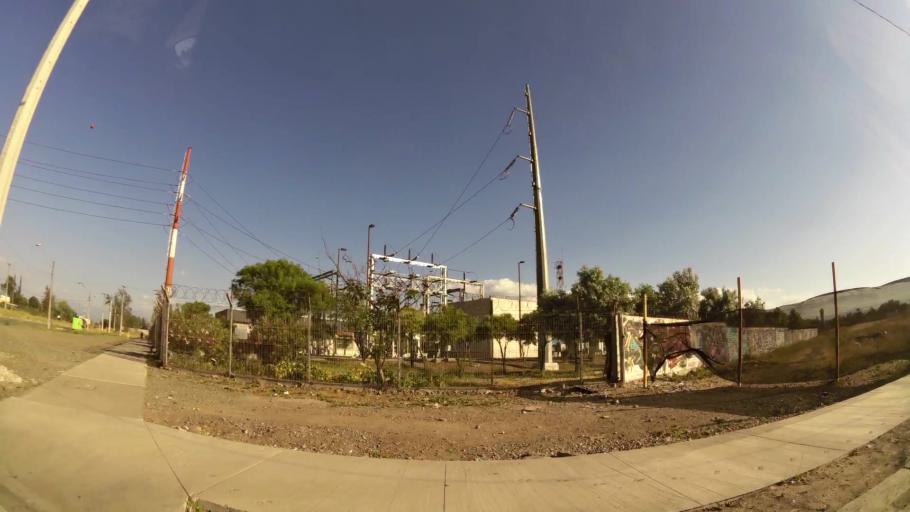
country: CL
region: Santiago Metropolitan
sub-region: Provincia de Maipo
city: San Bernardo
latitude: -33.5407
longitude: -70.7654
